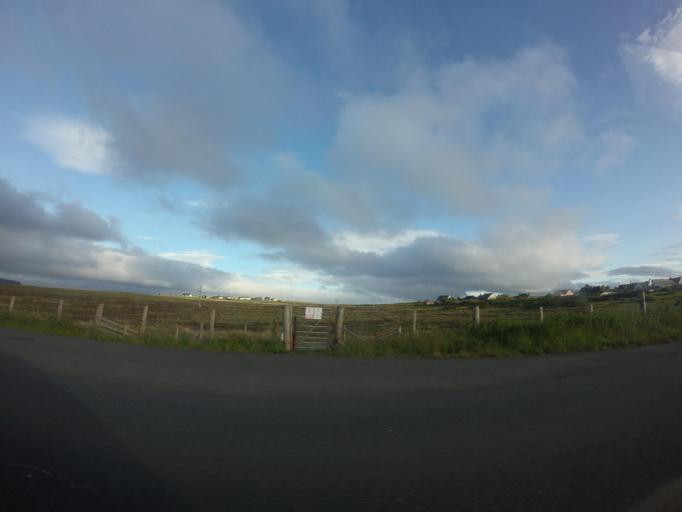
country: GB
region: Scotland
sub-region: Eilean Siar
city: Stornoway
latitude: 58.2030
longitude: -6.3353
